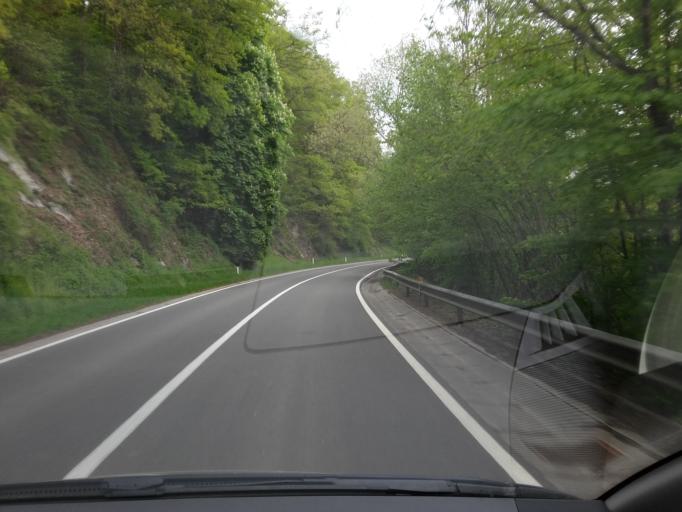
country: BE
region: Wallonia
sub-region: Province du Luxembourg
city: Neufchateau
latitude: 49.8366
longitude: 5.4241
